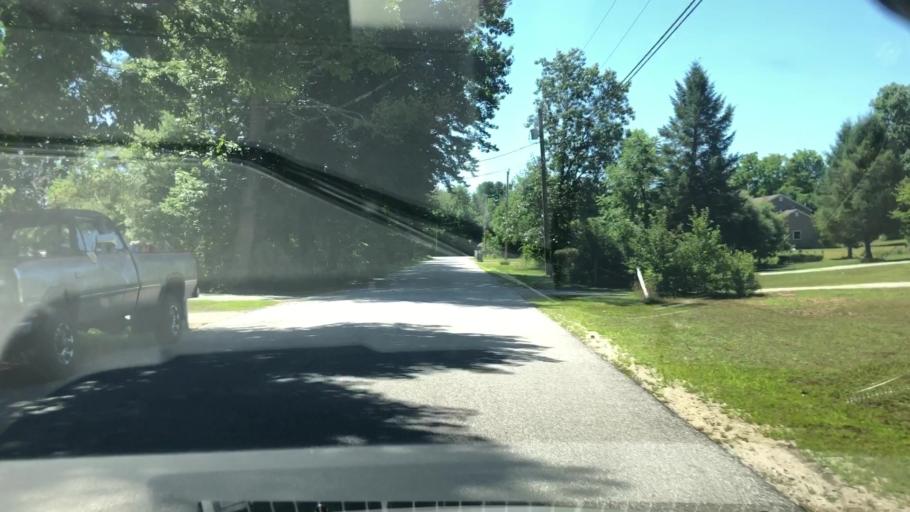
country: US
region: New Hampshire
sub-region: Hillsborough County
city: Milford
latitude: 42.8317
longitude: -71.5860
